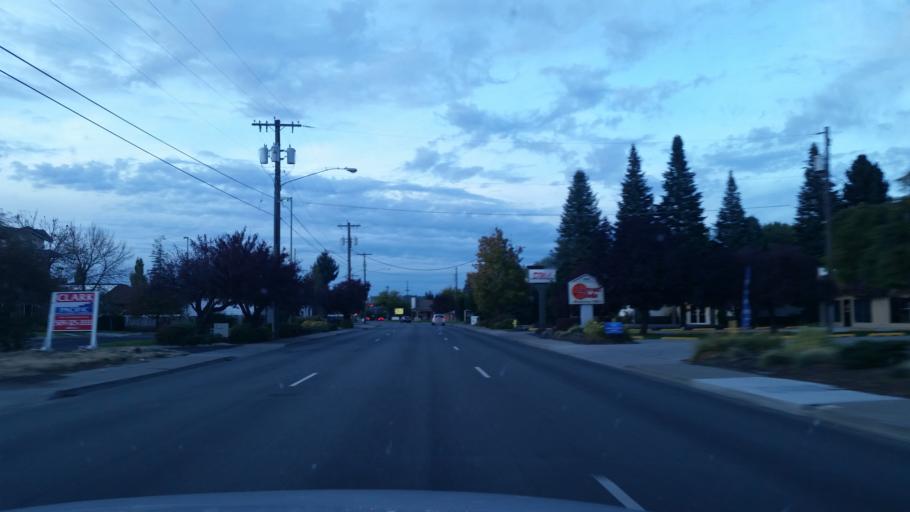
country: US
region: Washington
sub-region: Spokane County
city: Dishman
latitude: 47.6614
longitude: -117.2815
